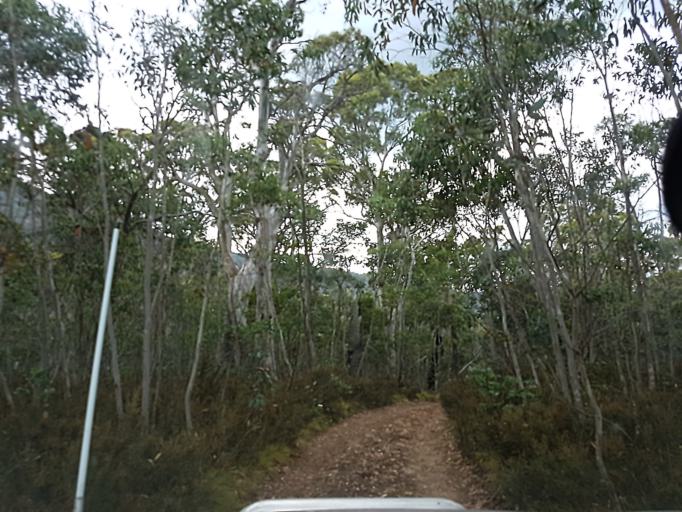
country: AU
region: New South Wales
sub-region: Snowy River
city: Jindabyne
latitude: -36.8790
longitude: 148.1595
